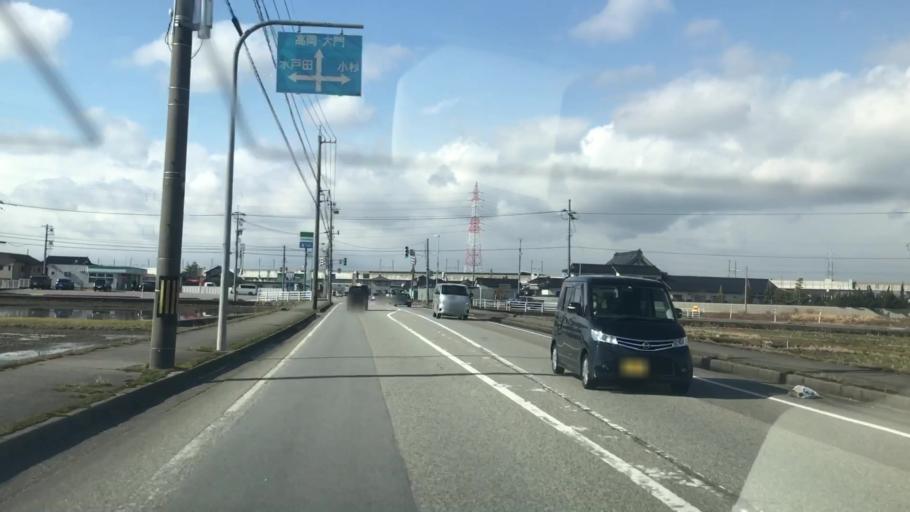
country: JP
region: Toyama
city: Nishishinminato
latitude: 36.7205
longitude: 137.0756
